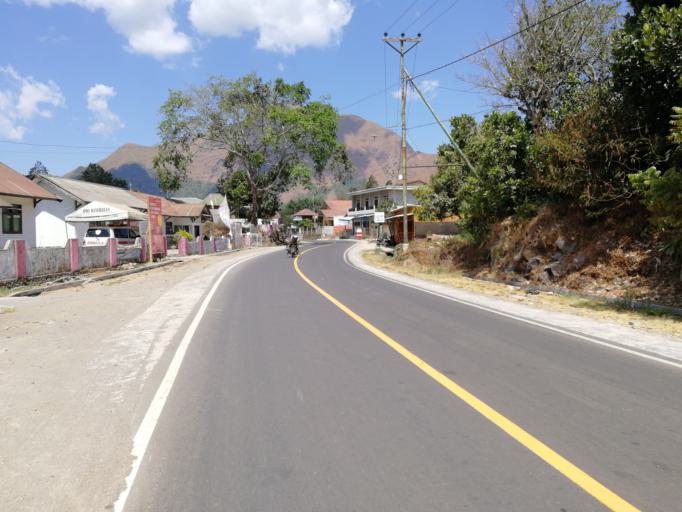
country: ID
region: West Nusa Tenggara
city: Sembalunlawang
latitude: -8.3599
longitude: 116.5315
